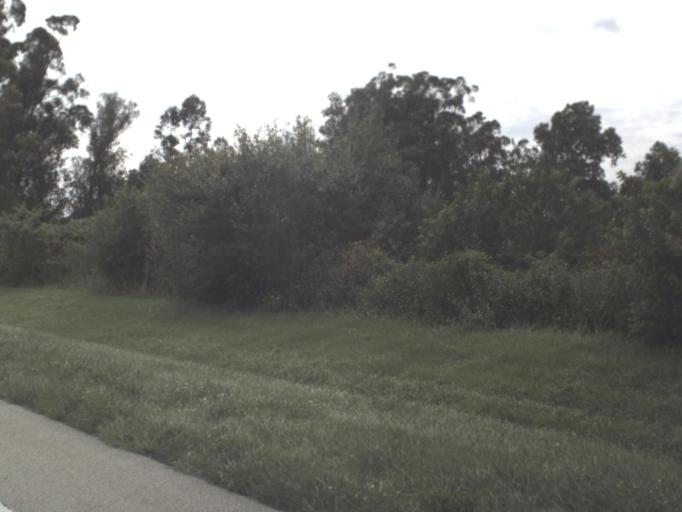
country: US
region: Florida
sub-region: DeSoto County
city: Southeast Arcadia
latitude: 27.1124
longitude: -81.7948
